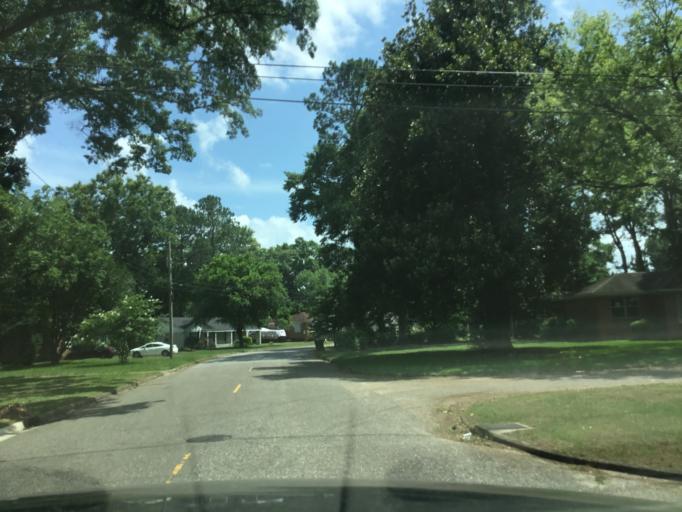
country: US
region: Alabama
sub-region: Montgomery County
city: Montgomery
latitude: 32.3869
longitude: -86.2587
